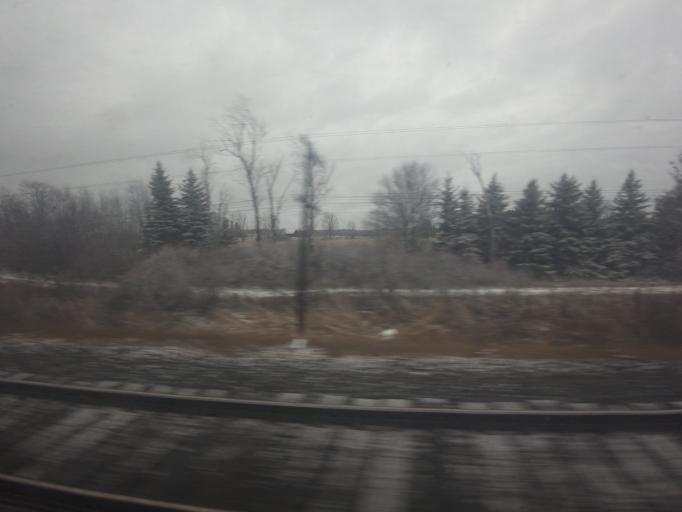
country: CA
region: Ontario
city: Gananoque
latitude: 44.3840
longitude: -76.0633
